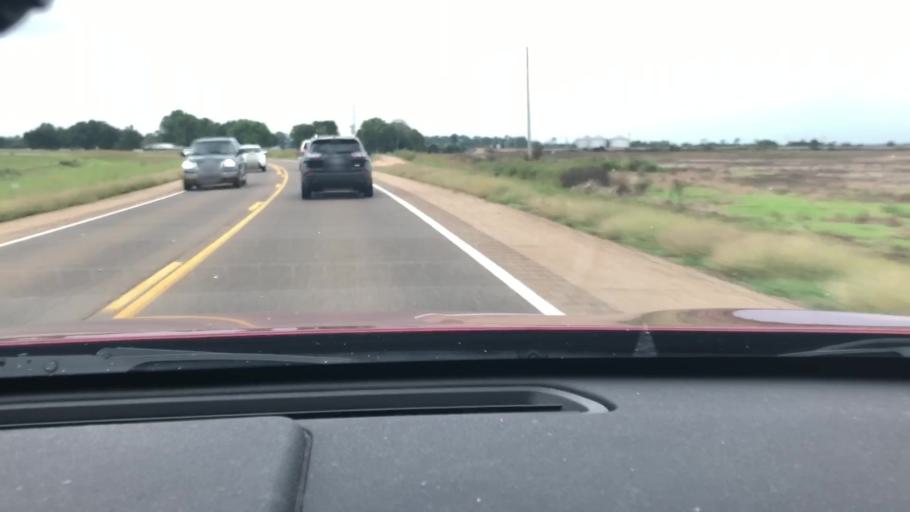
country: US
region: Arkansas
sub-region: Lafayette County
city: Lewisville
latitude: 33.3798
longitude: -93.7363
